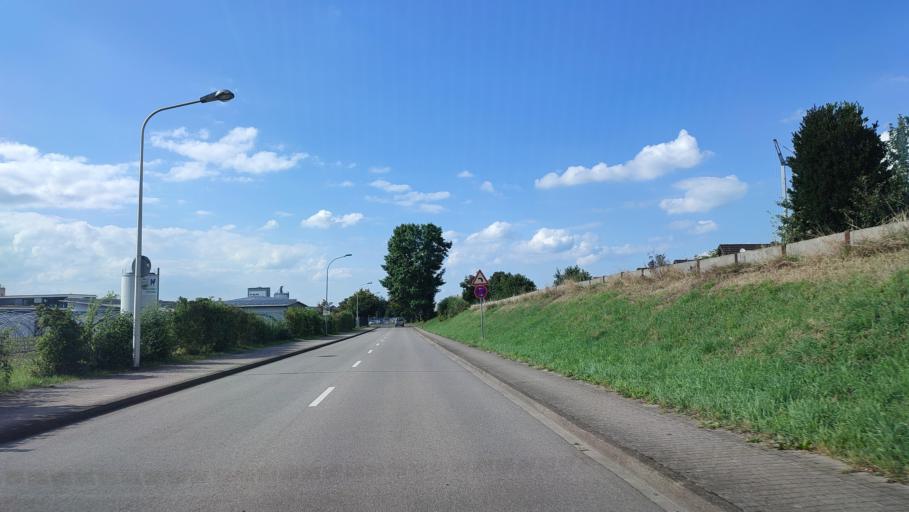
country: DE
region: Baden-Wuerttemberg
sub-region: Freiburg Region
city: Oberkirch
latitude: 48.5321
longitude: 8.0707
